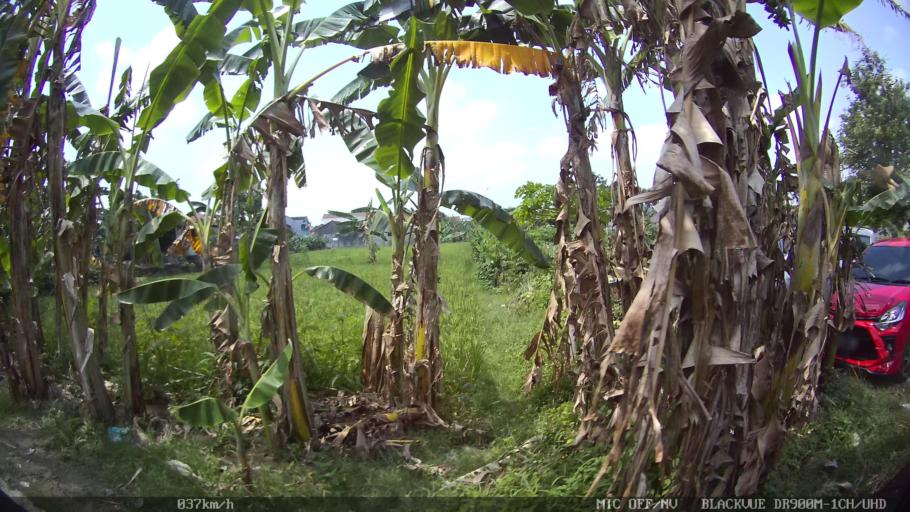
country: ID
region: Daerah Istimewa Yogyakarta
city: Yogyakarta
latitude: -7.8186
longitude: 110.3978
